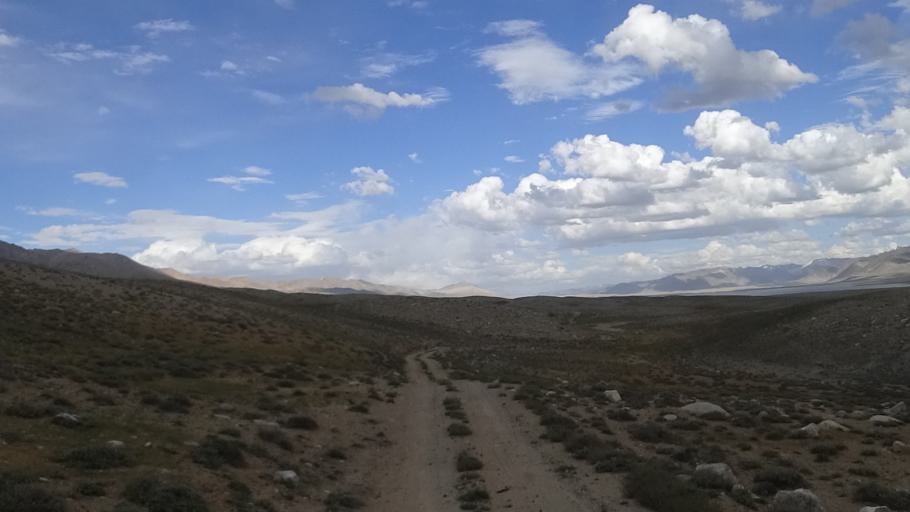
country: TJ
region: Gorno-Badakhshan
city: Murghob
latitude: 37.4689
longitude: 73.5987
